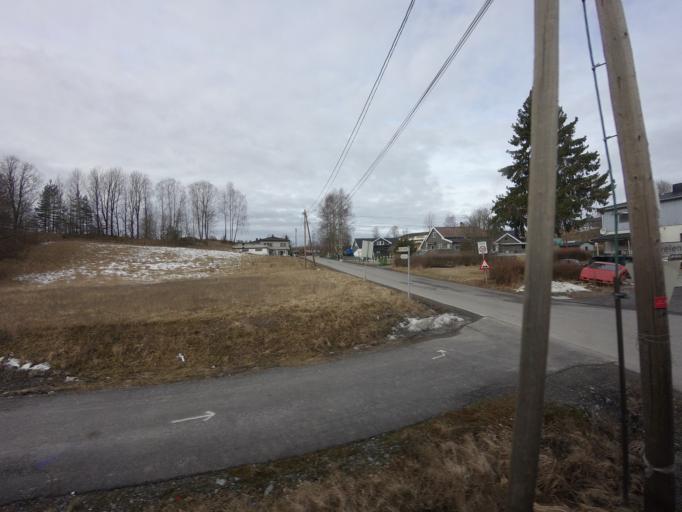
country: NO
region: Akershus
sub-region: Enebakk
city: Flateby
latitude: 59.8744
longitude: 11.2228
